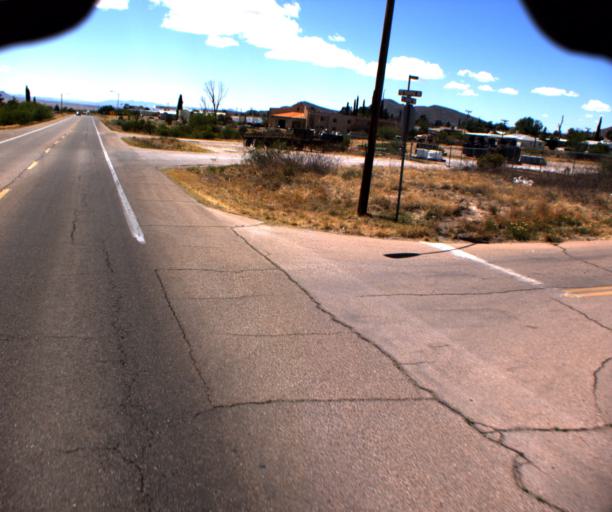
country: US
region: Arizona
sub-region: Cochise County
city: Bisbee
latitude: 31.3994
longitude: -109.9238
